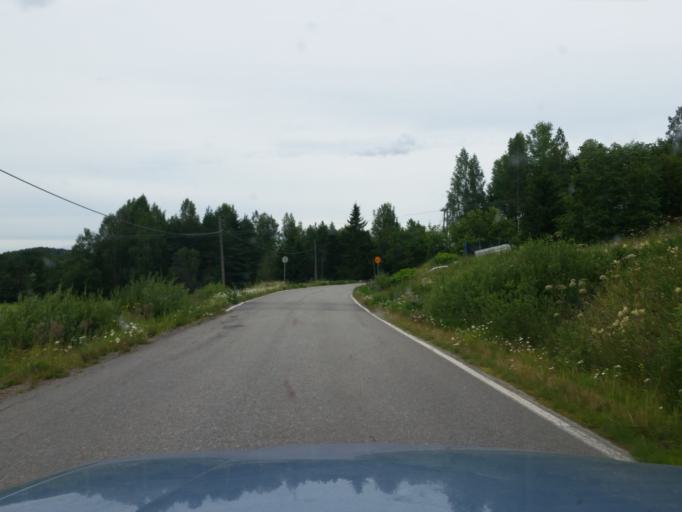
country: FI
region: Uusimaa
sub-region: Helsinki
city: Sammatti
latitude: 60.4563
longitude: 23.8464
